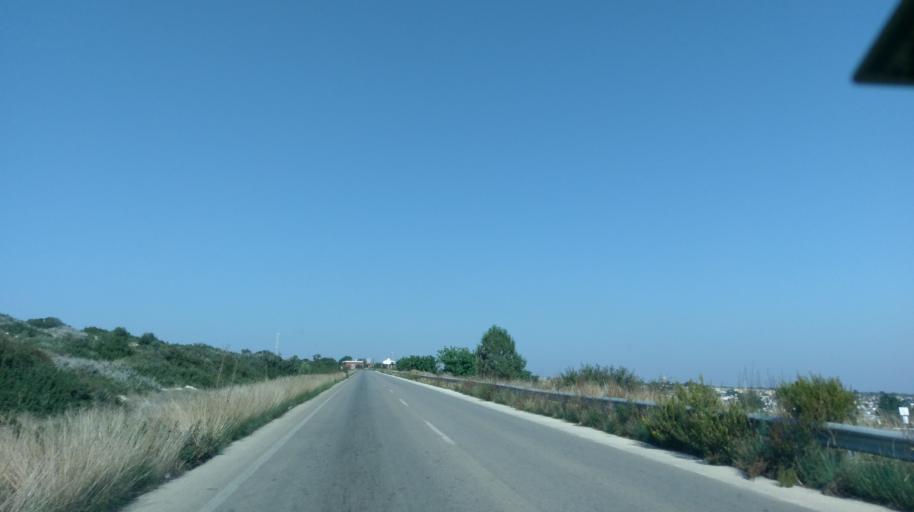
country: CY
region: Ammochostos
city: Leonarisso
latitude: 35.4263
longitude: 34.1271
